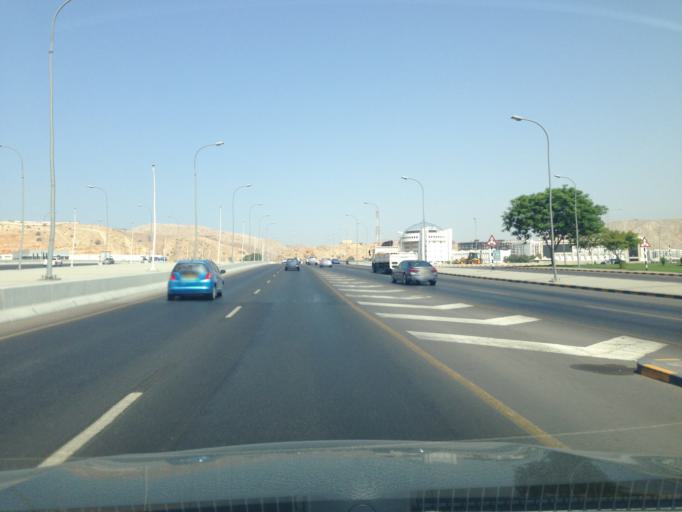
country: OM
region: Muhafazat Masqat
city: Muscat
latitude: 23.6108
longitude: 58.4949
